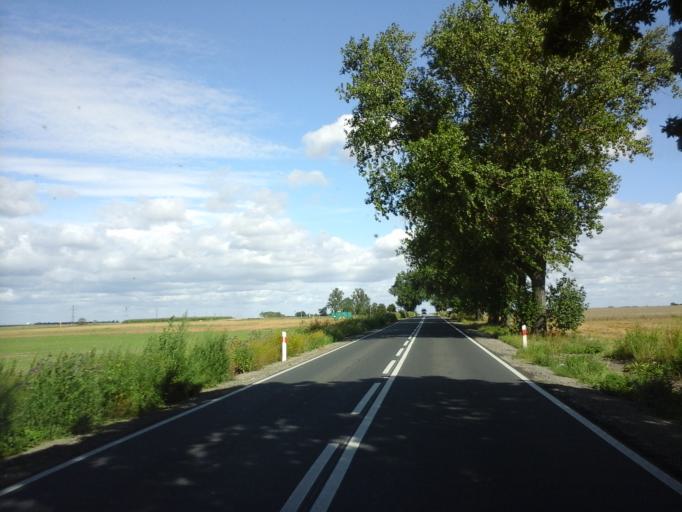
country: PL
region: West Pomeranian Voivodeship
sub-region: Powiat stargardzki
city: Stargard Szczecinski
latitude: 53.2562
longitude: 15.1000
